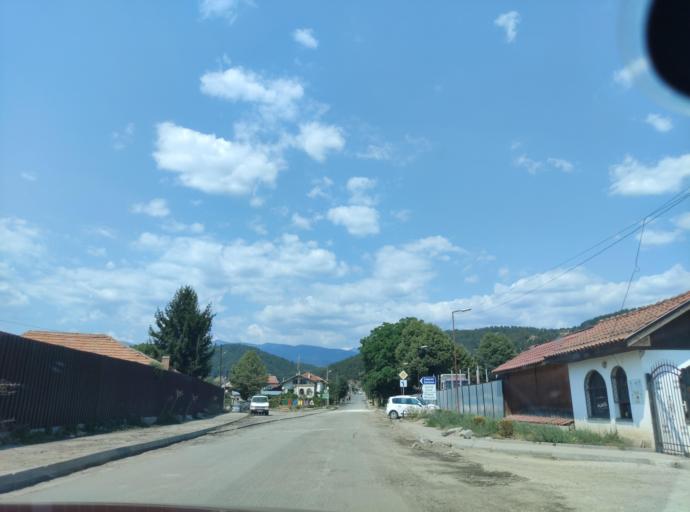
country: BG
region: Blagoevgrad
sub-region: Obshtina Belitsa
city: Belitsa
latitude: 41.9438
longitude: 23.5655
